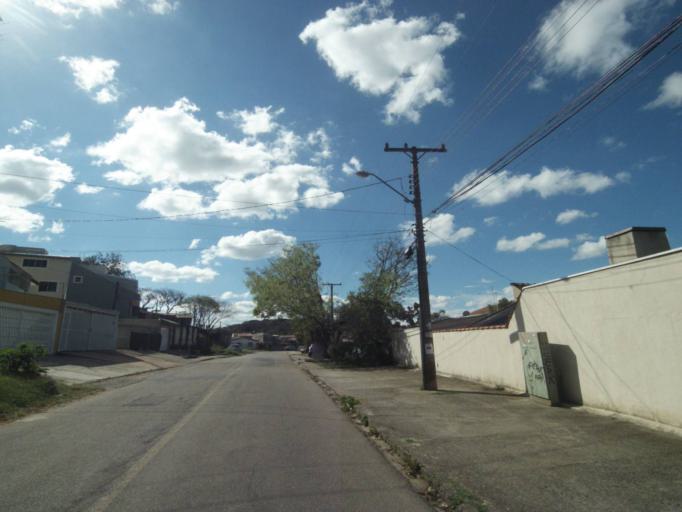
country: BR
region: Parana
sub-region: Curitiba
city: Curitiba
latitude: -25.3822
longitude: -49.2489
